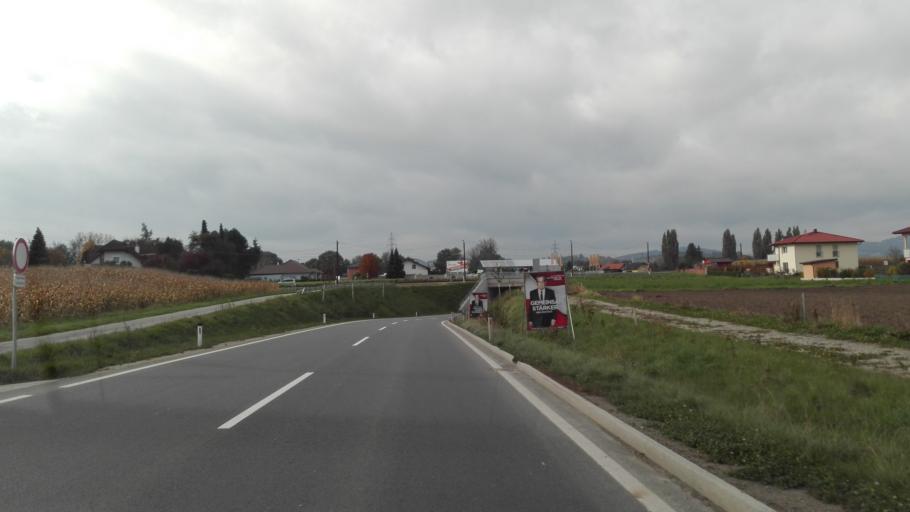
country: AT
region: Upper Austria
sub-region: Politischer Bezirk Urfahr-Umgebung
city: Feldkirchen an der Donau
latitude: 48.2961
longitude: 14.0276
